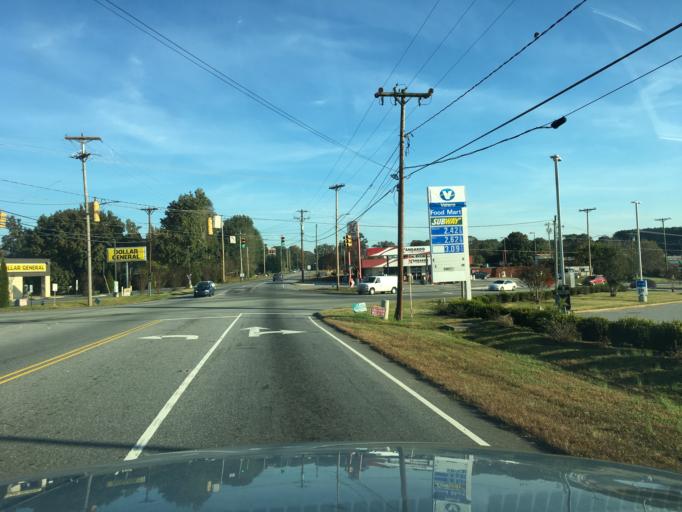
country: US
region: North Carolina
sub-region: Catawba County
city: Newton
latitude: 35.6445
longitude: -81.2693
